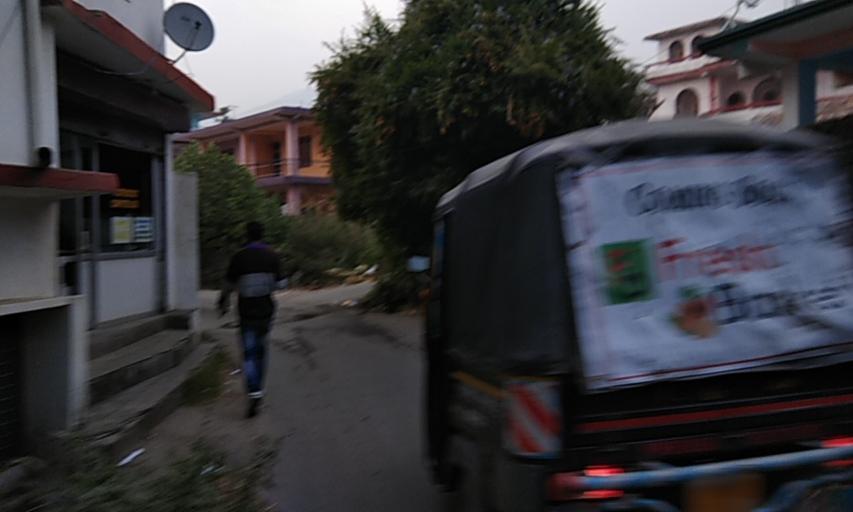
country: IN
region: Himachal Pradesh
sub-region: Kangra
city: Palampur
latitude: 32.1157
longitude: 76.5339
